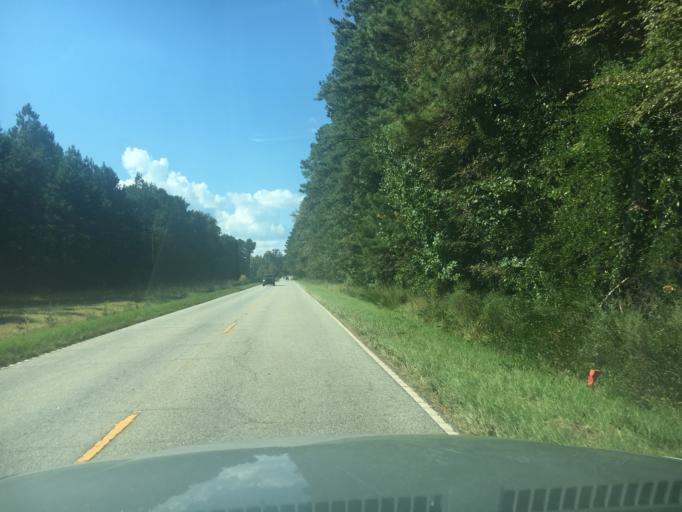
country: US
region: South Carolina
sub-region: Greenwood County
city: Greenwood
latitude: 34.2665
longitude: -82.1878
